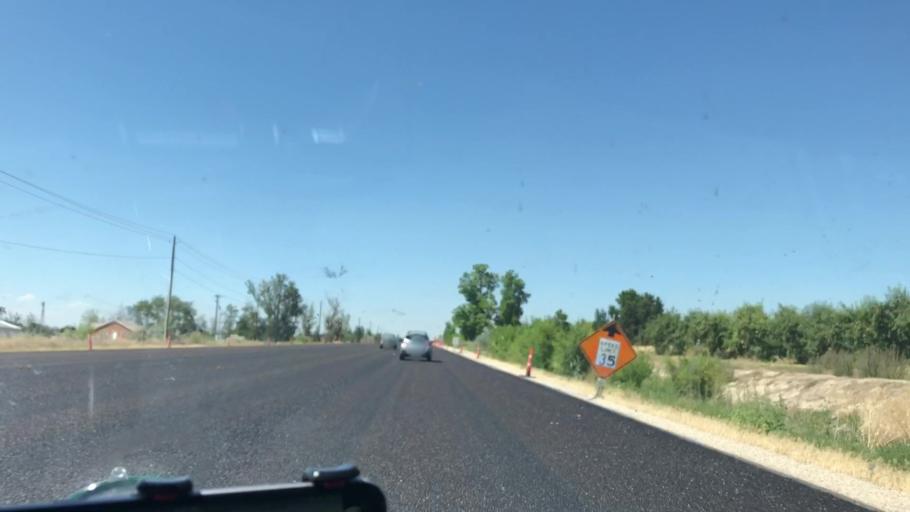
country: US
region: Idaho
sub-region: Owyhee County
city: Marsing
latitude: 43.5899
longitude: -116.7922
